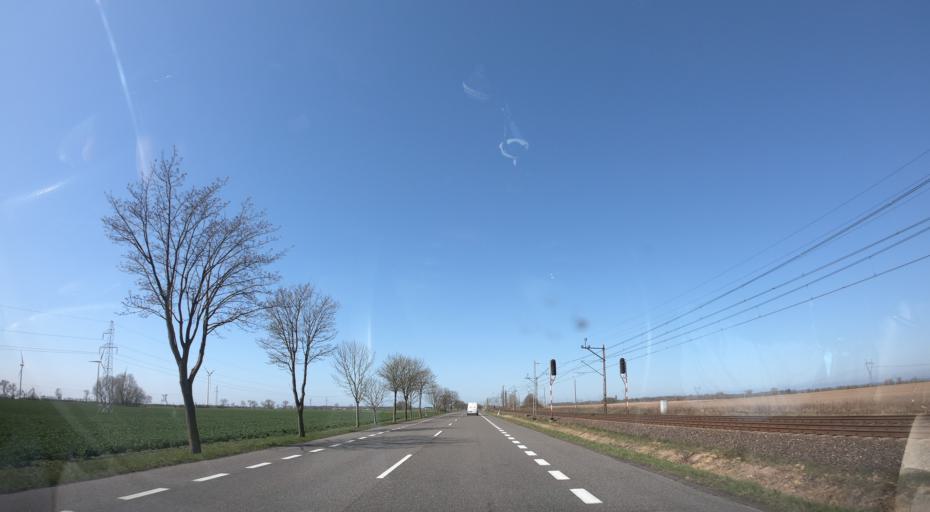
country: PL
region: West Pomeranian Voivodeship
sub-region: Powiat kamienski
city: Wolin
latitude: 53.8461
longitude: 14.6602
